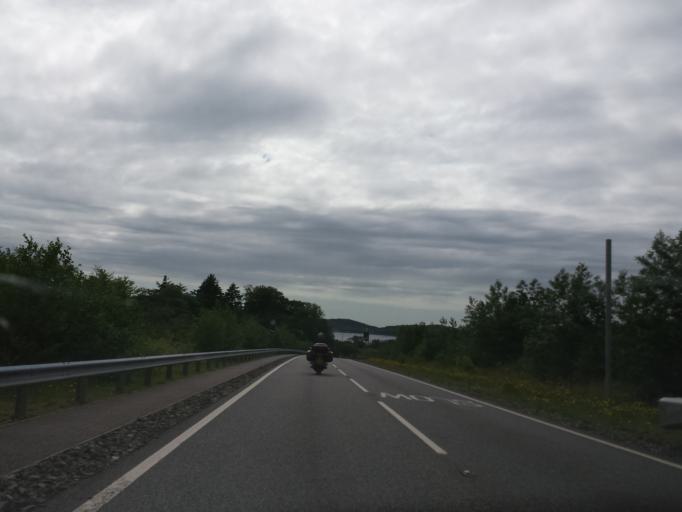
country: GB
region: Scotland
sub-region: Argyll and Bute
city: Isle Of Mull
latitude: 56.9119
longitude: -5.8281
